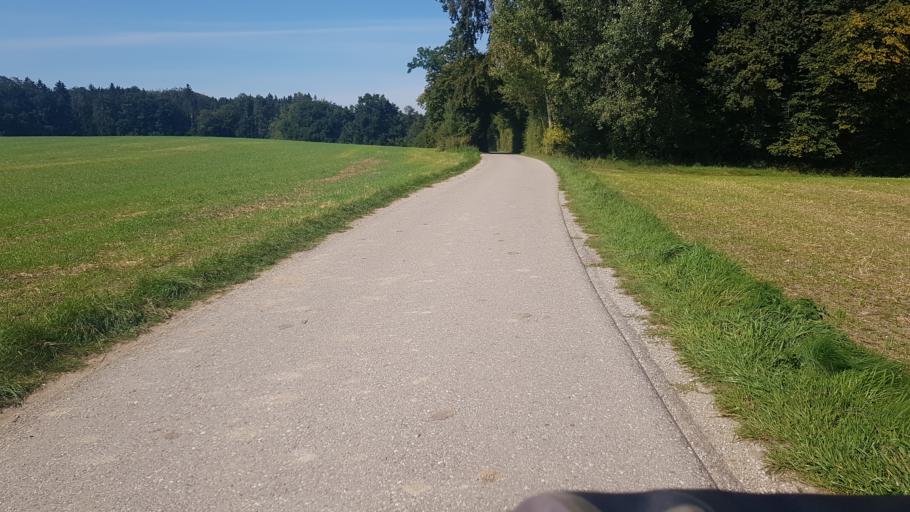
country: DE
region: Bavaria
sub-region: Upper Bavaria
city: Herrsching am Ammersee
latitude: 48.0174
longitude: 11.1588
